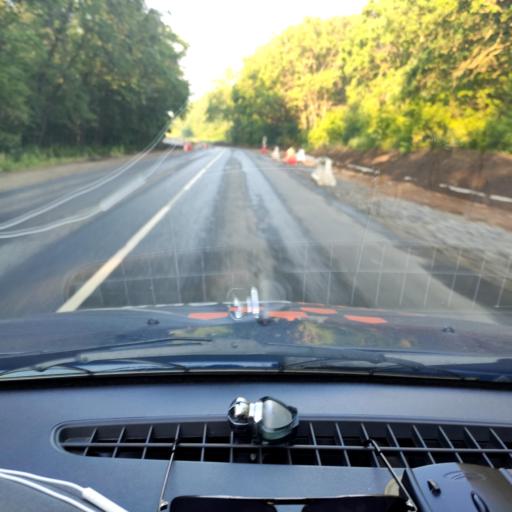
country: RU
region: Lipetsk
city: Kazaki
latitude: 52.5122
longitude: 38.0984
